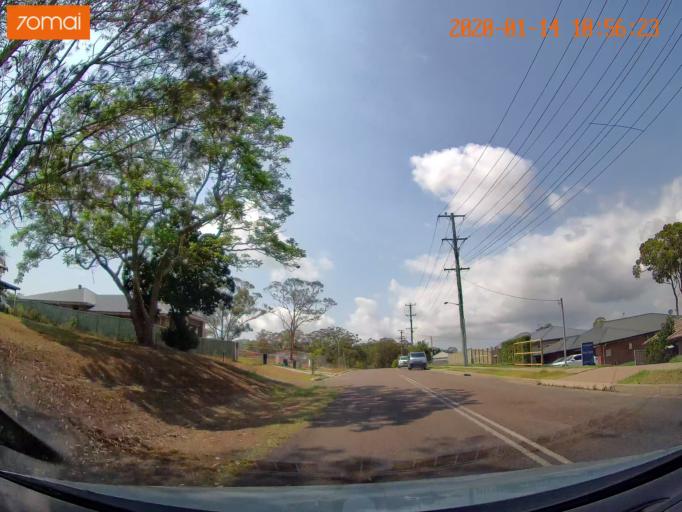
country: AU
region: New South Wales
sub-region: Lake Macquarie Shire
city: Dora Creek
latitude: -33.0996
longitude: 151.4874
